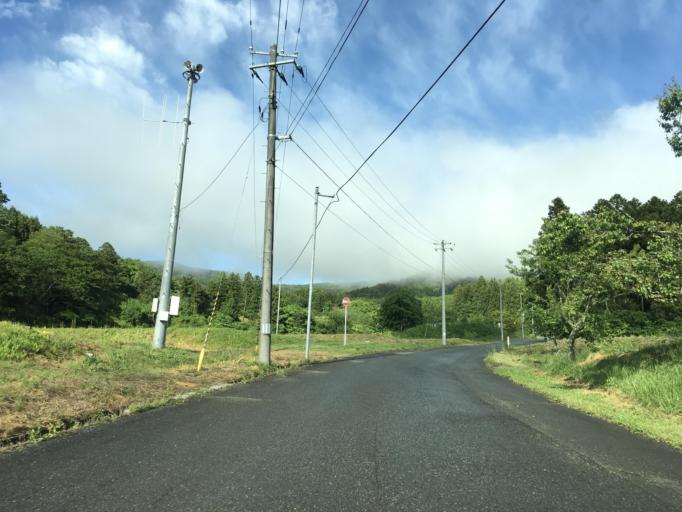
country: JP
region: Iwate
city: Ichinoseki
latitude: 38.8638
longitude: 141.4301
